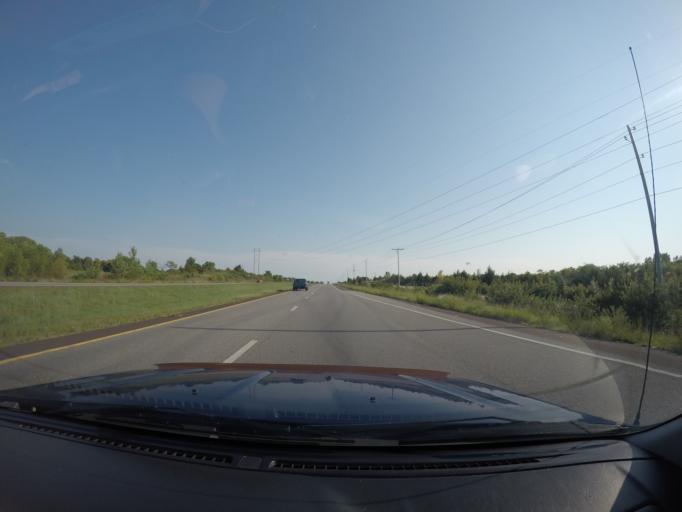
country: US
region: Kansas
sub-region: Wyandotte County
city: Bonner Springs
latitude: 38.9913
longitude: -94.8532
